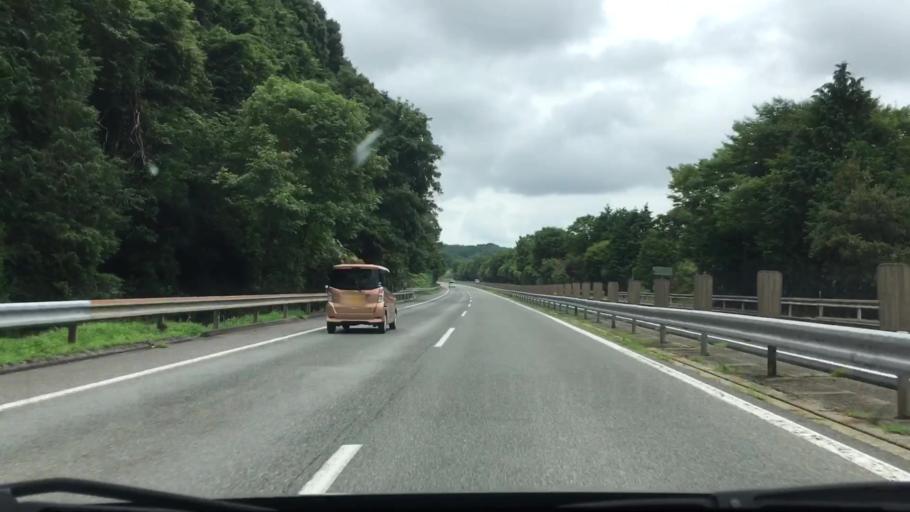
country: JP
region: Hiroshima
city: Miyoshi
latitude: 34.7649
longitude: 132.7931
